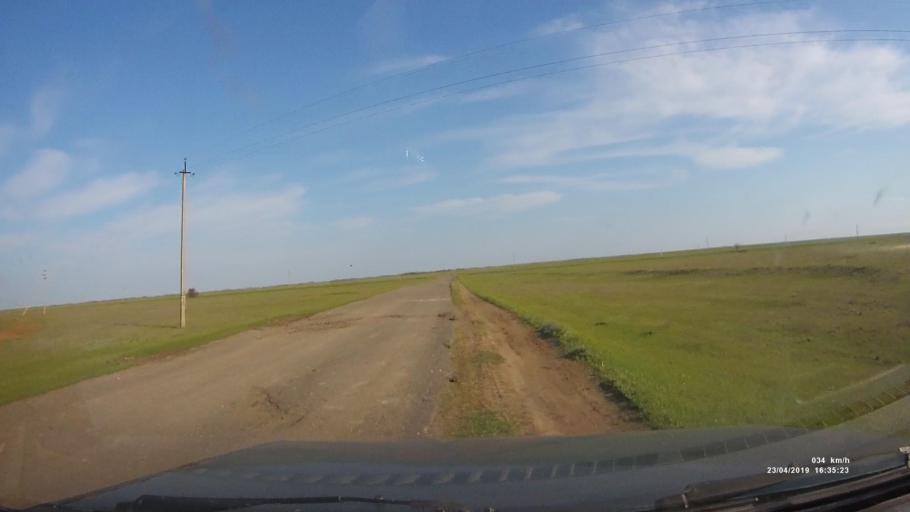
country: RU
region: Kalmykiya
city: Priyutnoye
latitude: 46.3310
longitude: 43.1372
